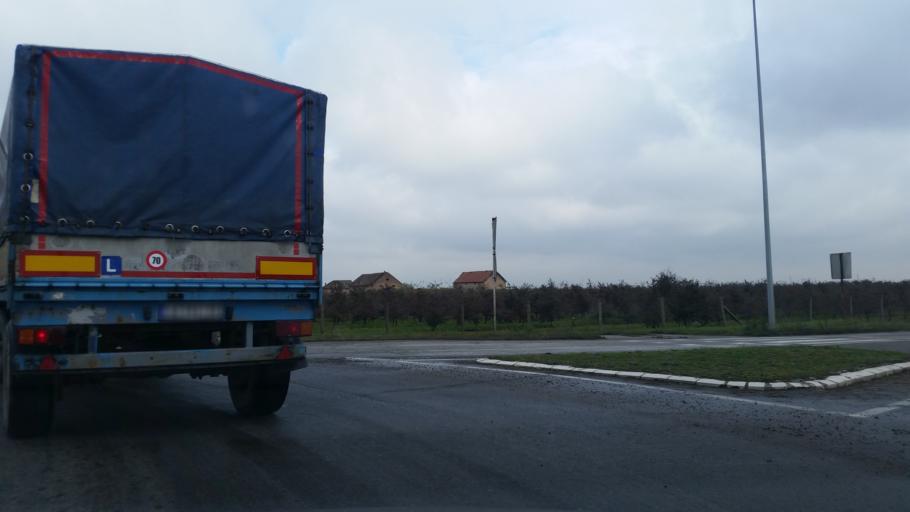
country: RS
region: Autonomna Pokrajina Vojvodina
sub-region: Srednjebanatski Okrug
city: Zrenjanin
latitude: 45.4015
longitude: 20.3769
